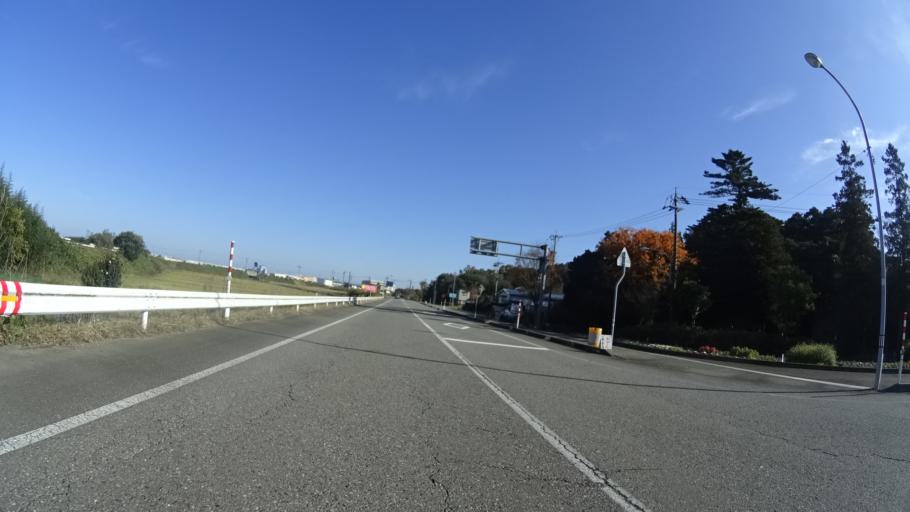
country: JP
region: Ishikawa
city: Komatsu
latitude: 36.3139
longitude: 136.3893
